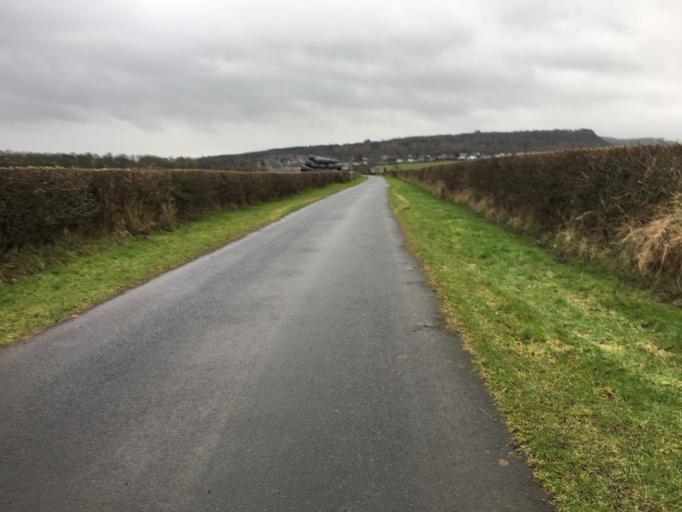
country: GB
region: Scotland
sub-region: Stirling
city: Stirling
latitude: 56.1222
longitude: -3.9754
